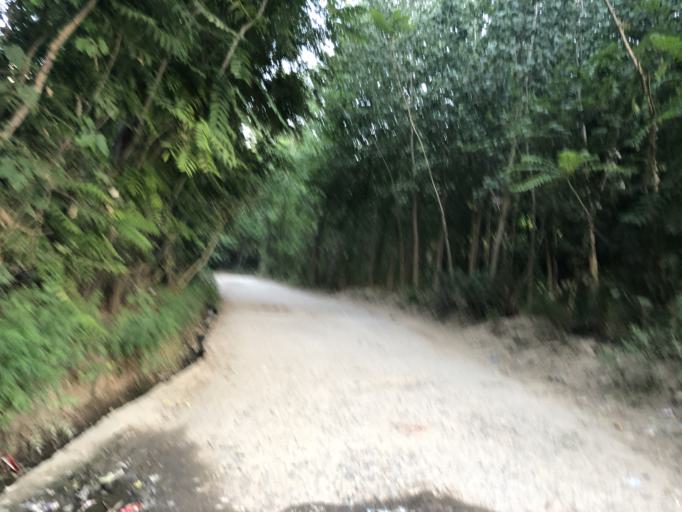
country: PK
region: Khyber Pakhtunkhwa
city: Daggar
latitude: 34.5798
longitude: 72.4548
